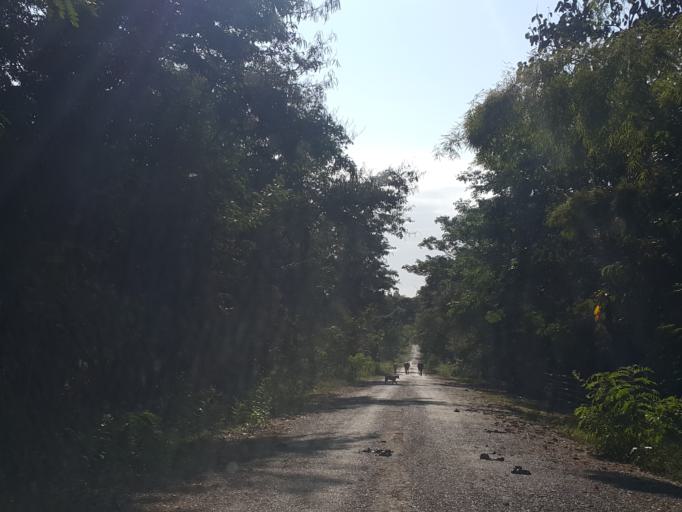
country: TH
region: Lampang
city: Mae Mo
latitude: 18.3104
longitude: 99.6569
